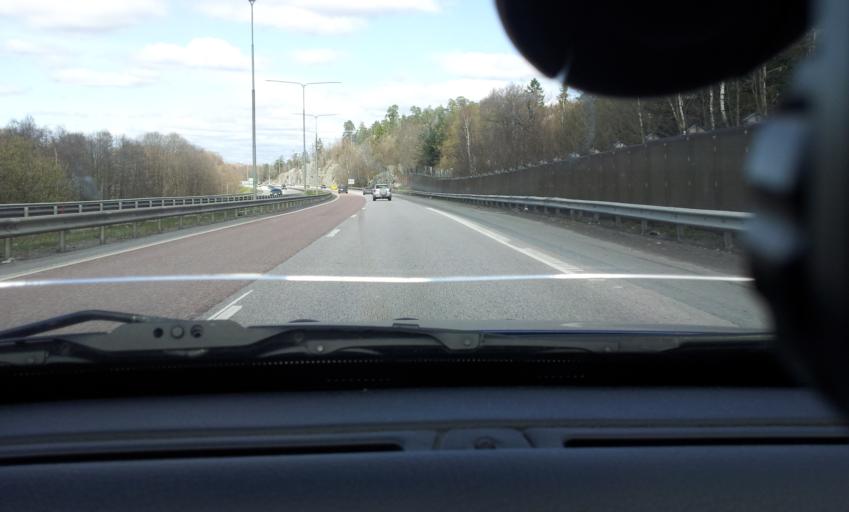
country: SE
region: Stockholm
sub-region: Nacka Kommun
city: Alta
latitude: 59.2354
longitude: 18.1231
